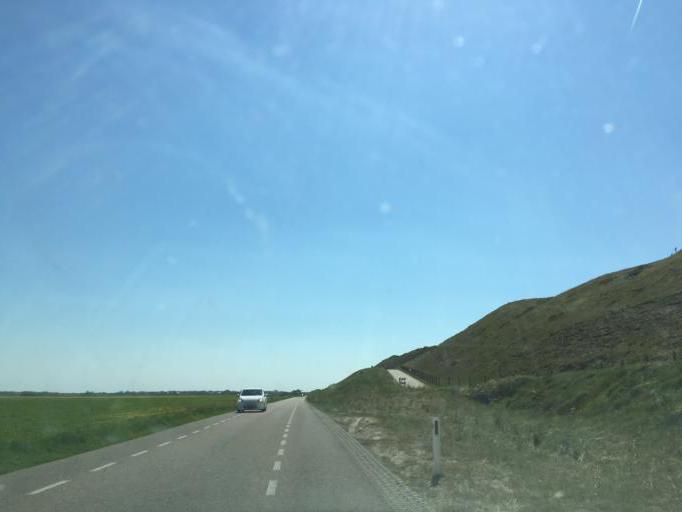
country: NL
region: North Holland
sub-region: Gemeente Den Helder
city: Den Helder
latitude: 52.8794
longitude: 4.7153
